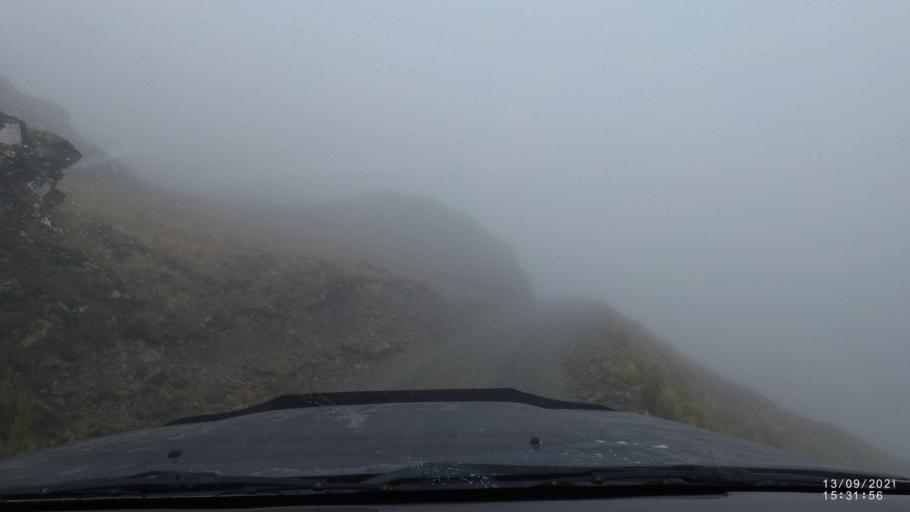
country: BO
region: Cochabamba
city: Colomi
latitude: -17.3396
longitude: -65.7497
